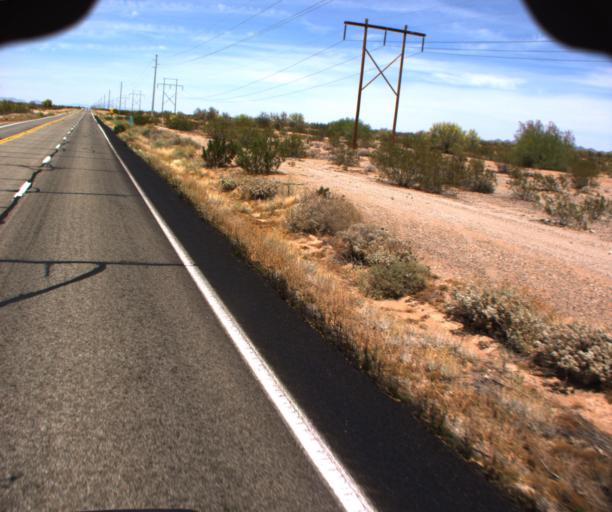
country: US
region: Arizona
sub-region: La Paz County
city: Quartzsite
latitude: 33.7820
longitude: -114.2170
